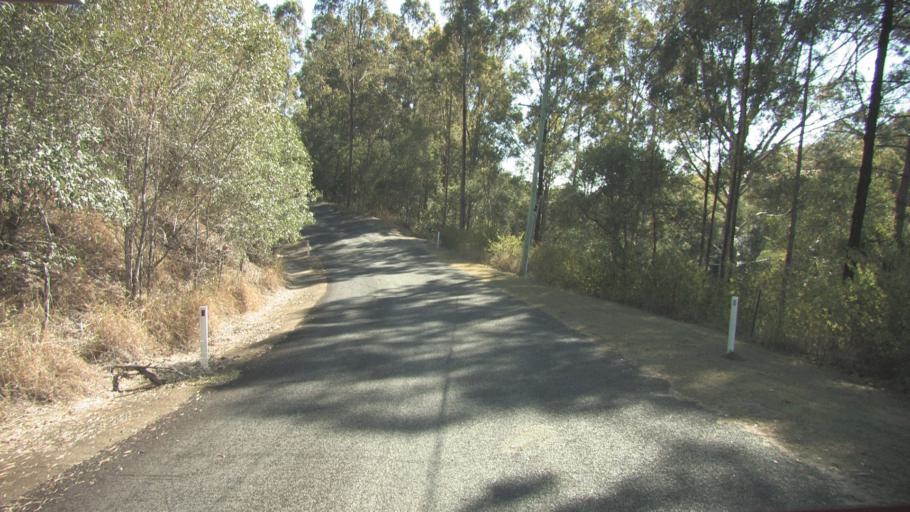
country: AU
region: Queensland
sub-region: Logan
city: Cedar Vale
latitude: -27.8970
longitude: 153.0214
